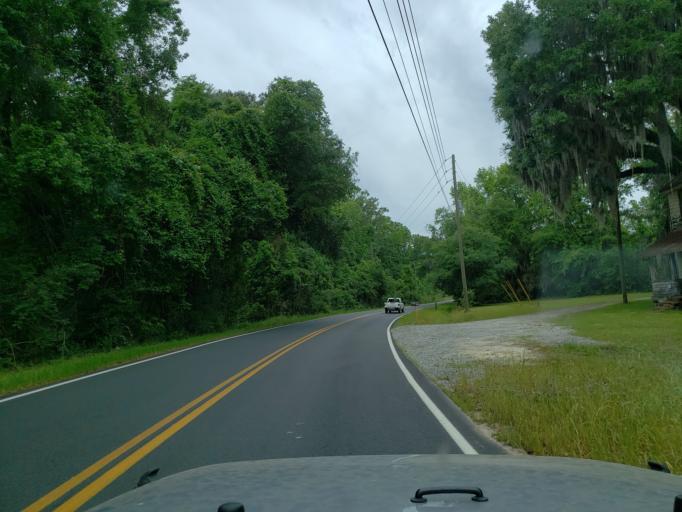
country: US
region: Georgia
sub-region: Chatham County
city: Port Wentworth
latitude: 32.1804
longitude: -81.2083
